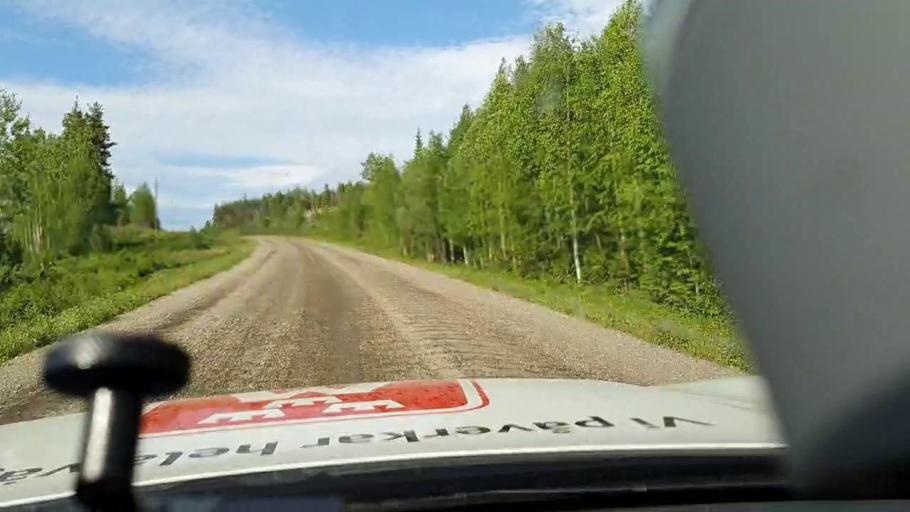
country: SE
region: Norrbotten
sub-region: Alvsbyns Kommun
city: AElvsbyn
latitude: 66.1654
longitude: 21.0561
